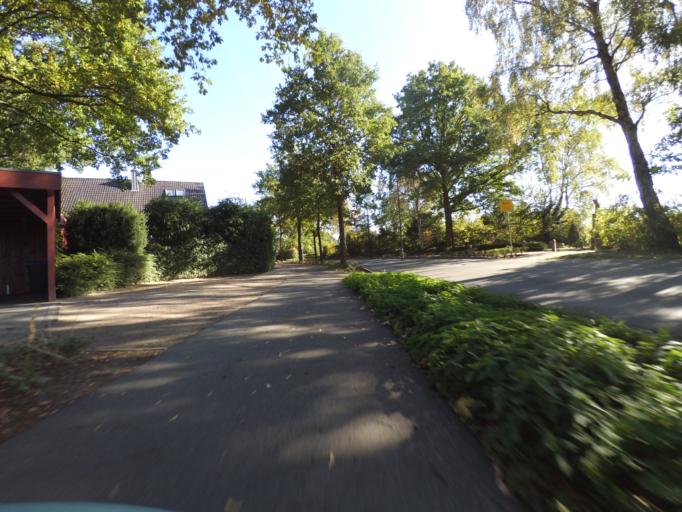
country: DE
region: North Rhine-Westphalia
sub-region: Regierungsbezirk Dusseldorf
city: Bocholt
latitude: 51.8880
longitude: 6.6565
